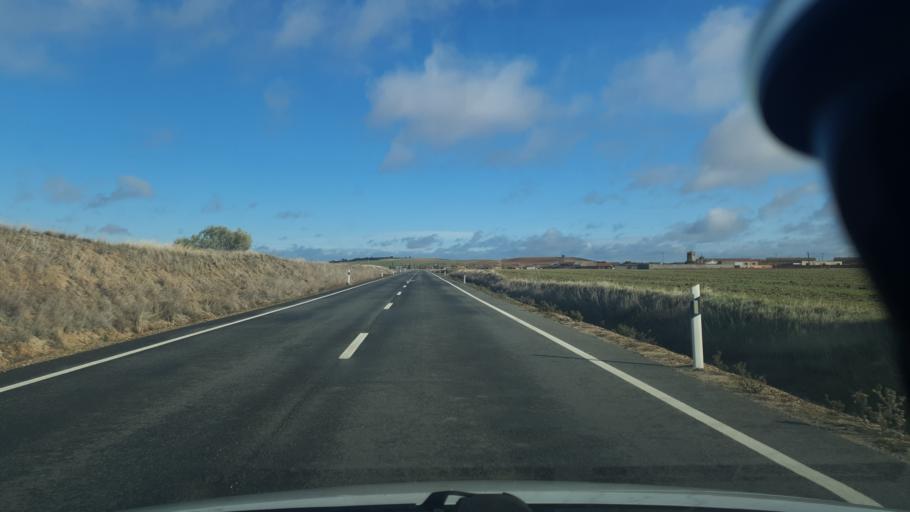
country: ES
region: Castille and Leon
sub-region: Provincia de Segovia
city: Codorniz
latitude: 41.0633
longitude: -4.6095
